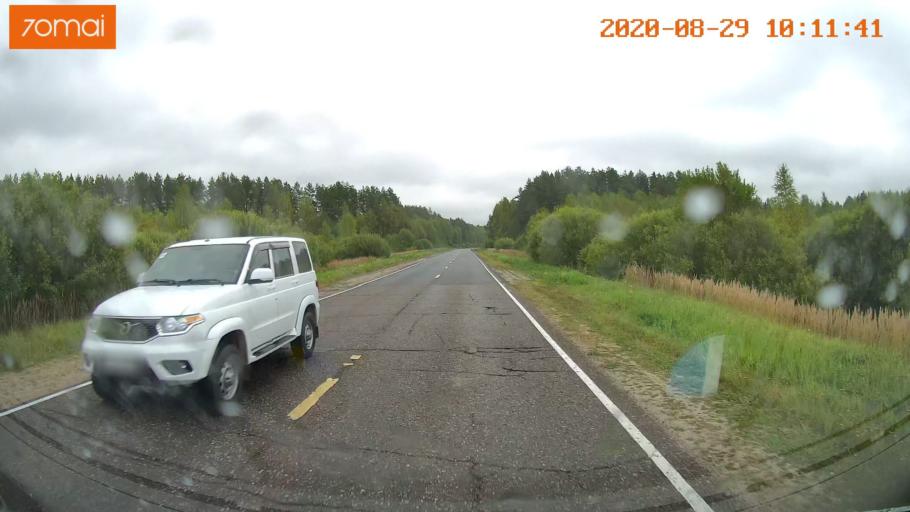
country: RU
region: Ivanovo
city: Kuznechikha
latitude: 57.3750
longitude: 42.6899
